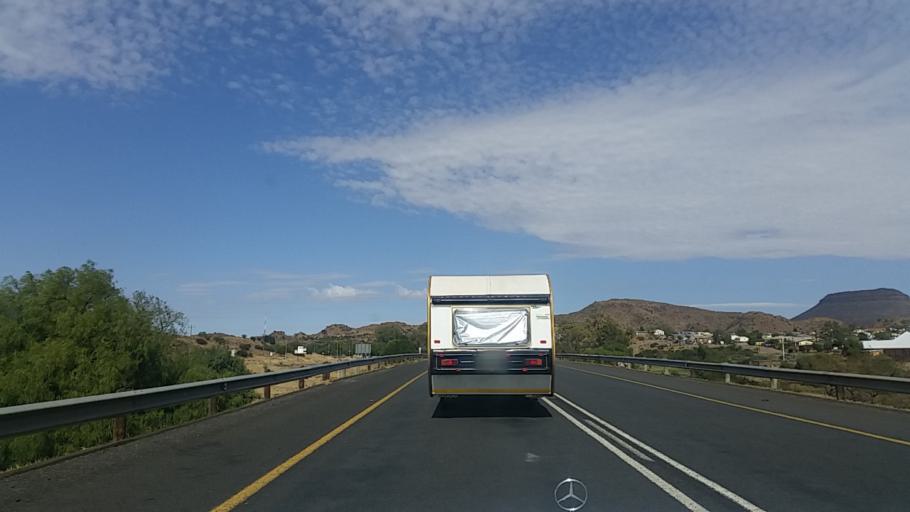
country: ZA
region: Northern Cape
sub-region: Pixley ka Seme District Municipality
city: Colesberg
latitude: -30.7094
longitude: 25.1060
